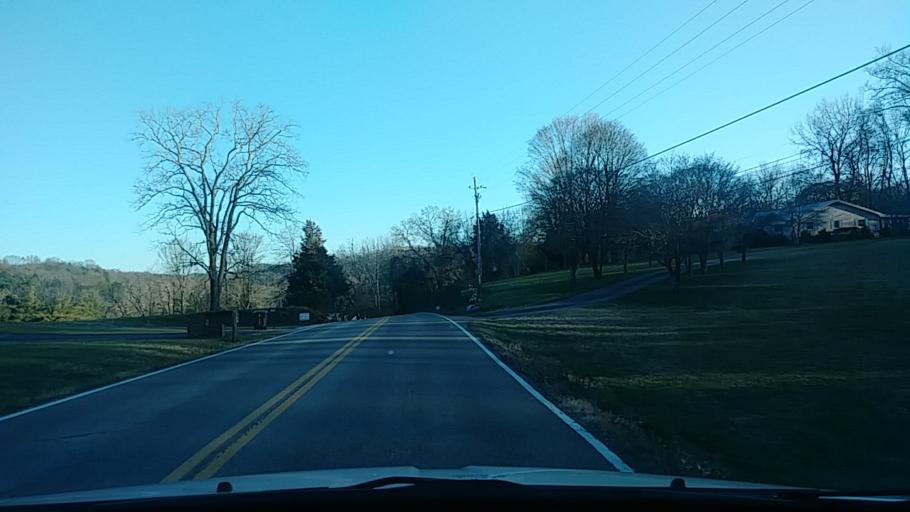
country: US
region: Tennessee
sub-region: Hamblen County
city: Morristown
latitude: 36.1981
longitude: -83.3990
